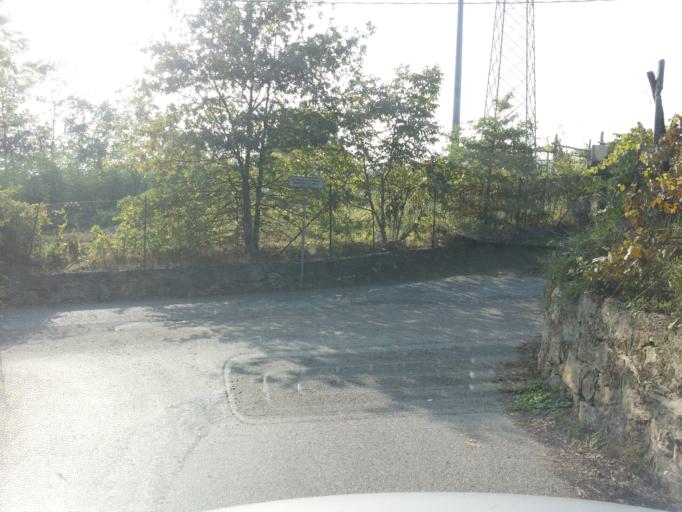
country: IT
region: Piedmont
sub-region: Provincia di Biella
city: Viverone
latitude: 45.4340
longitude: 8.0425
